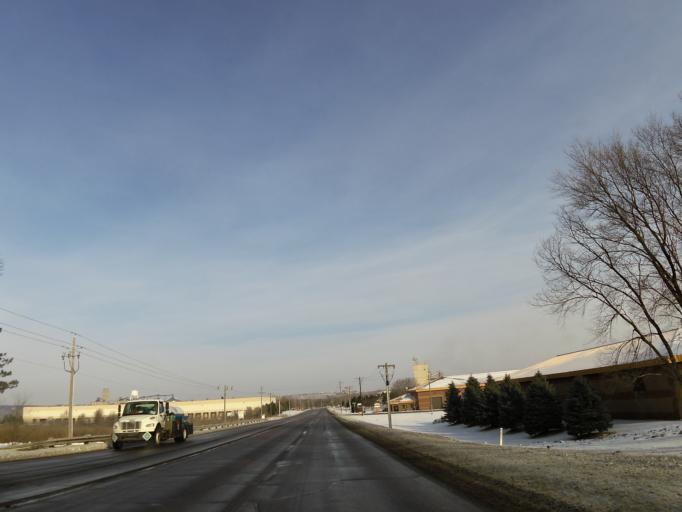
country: US
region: Minnesota
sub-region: Scott County
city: Shakopee
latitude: 44.7934
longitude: -93.4698
